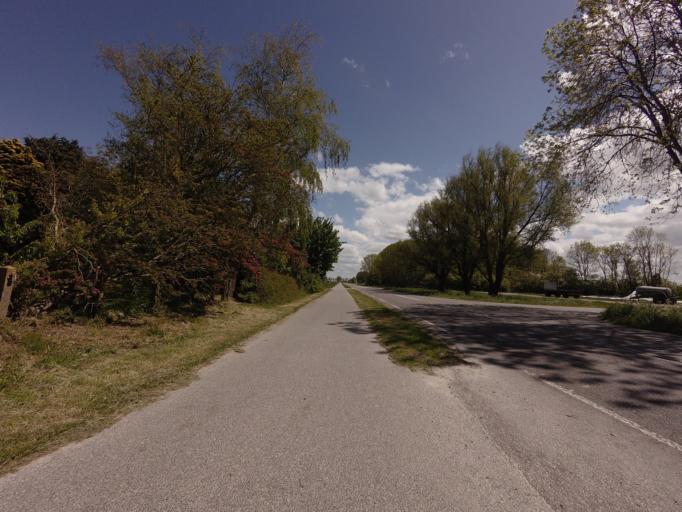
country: NL
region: Friesland
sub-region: Gemeente Harlingen
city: Harlingen
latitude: 53.1370
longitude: 5.4550
